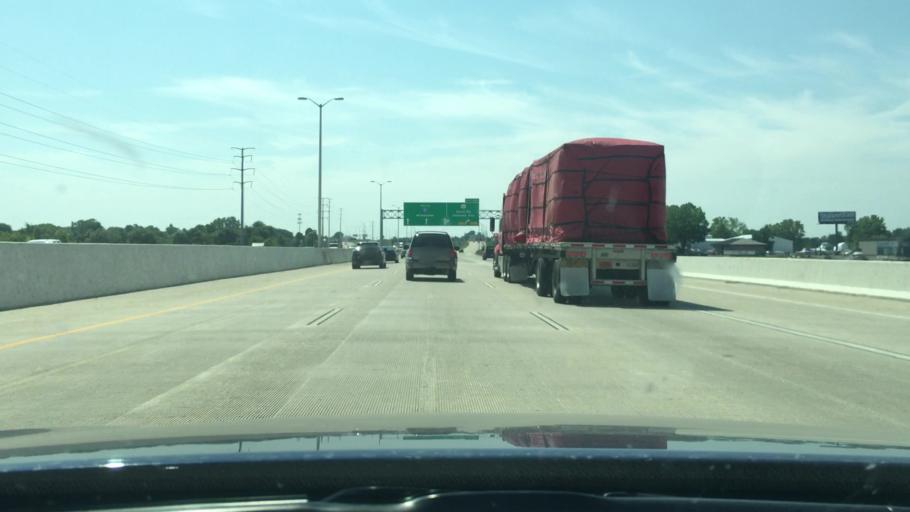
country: US
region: Wisconsin
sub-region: Winnebago County
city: Oshkosh
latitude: 44.0398
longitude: -88.5836
